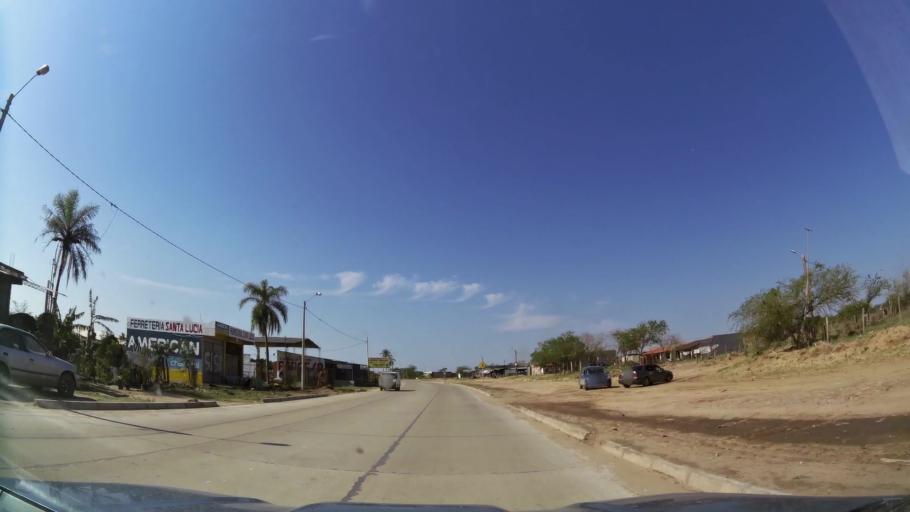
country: BO
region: Santa Cruz
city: Cotoca
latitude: -17.7217
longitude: -63.0771
